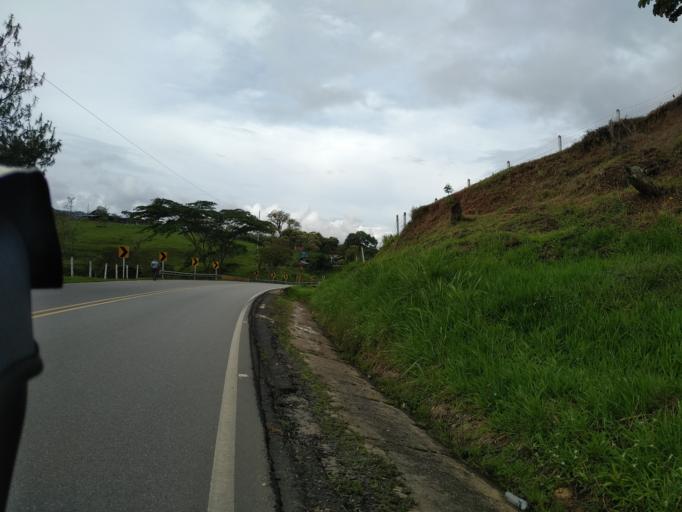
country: CO
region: Santander
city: Suaita
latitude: 6.1270
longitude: -73.3618
